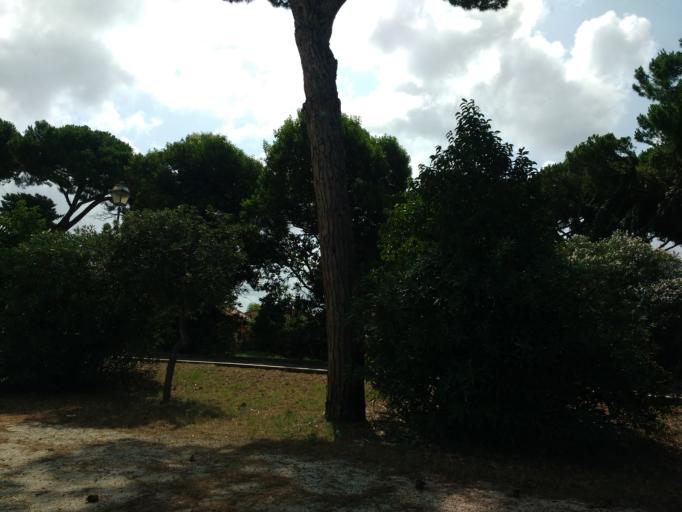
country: IT
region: Latium
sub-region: Citta metropolitana di Roma Capitale
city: Acilia-Castel Fusano-Ostia Antica
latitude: 41.7588
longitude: 12.2990
